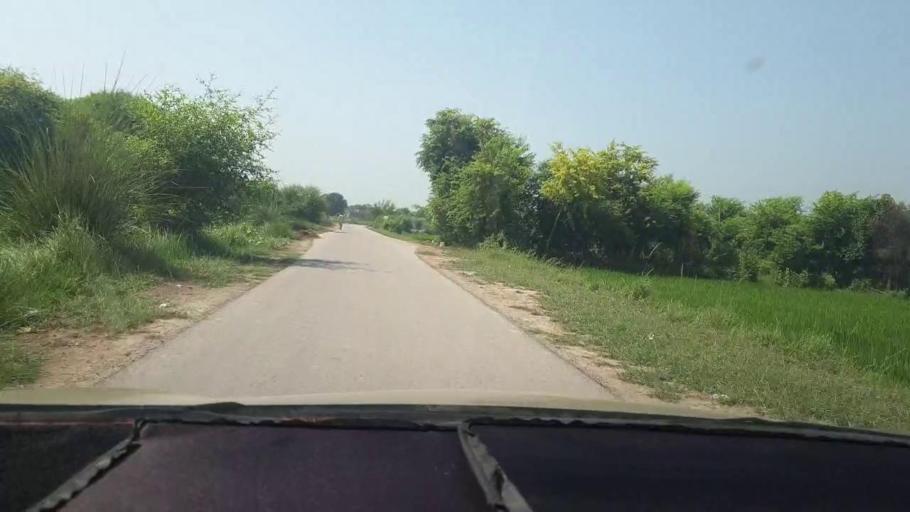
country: PK
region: Sindh
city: Kambar
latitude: 27.5838
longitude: 68.0477
